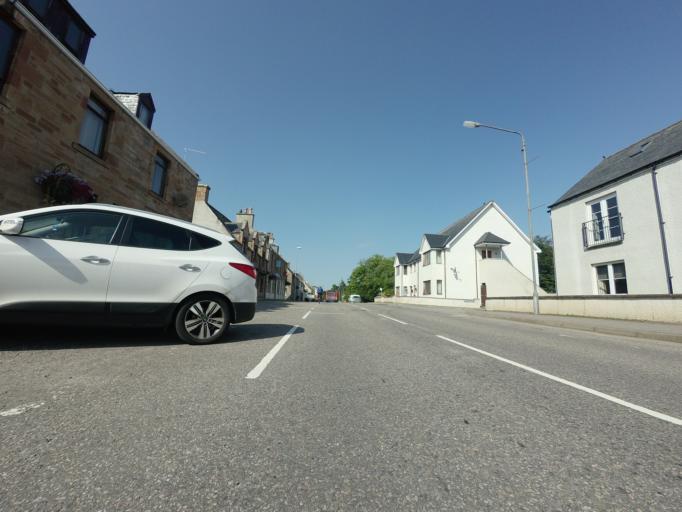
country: GB
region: Scotland
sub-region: Highland
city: Evanton
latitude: 57.6623
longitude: -4.3376
